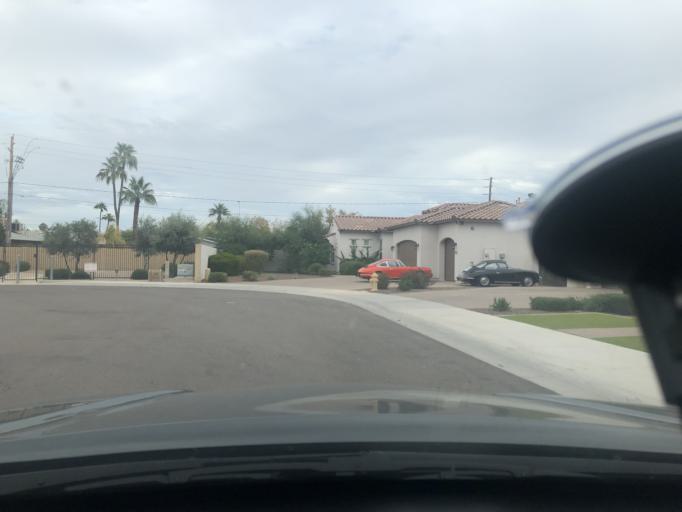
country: US
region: Arizona
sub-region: Maricopa County
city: Scottsdale
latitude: 33.4898
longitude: -111.8995
